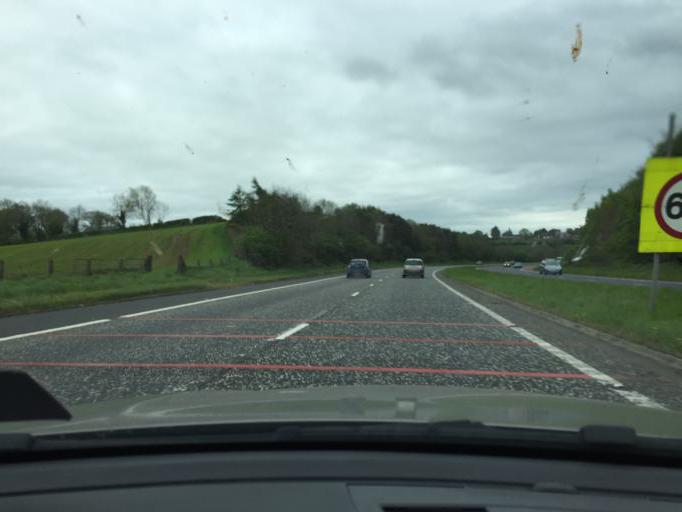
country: GB
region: Northern Ireland
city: Hillsborough
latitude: 54.4274
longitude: -6.1210
